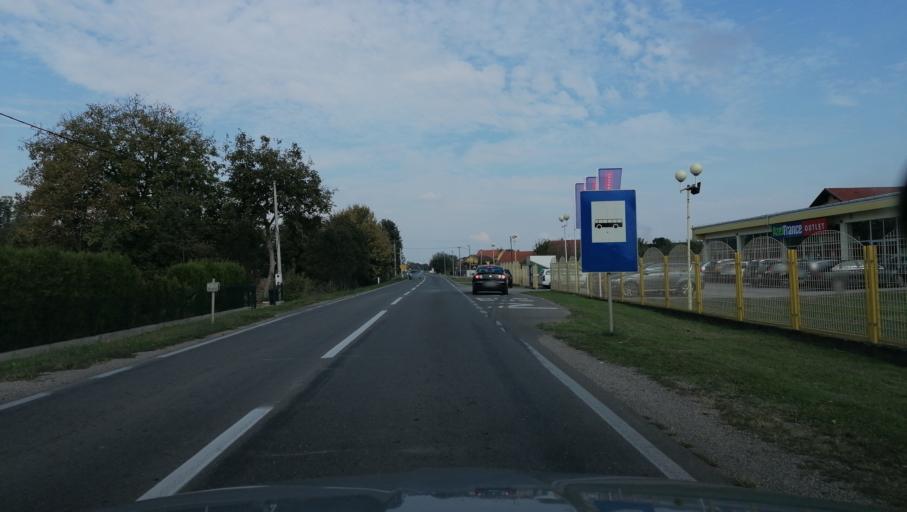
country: BA
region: Republika Srpska
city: Dvorovi
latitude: 44.8190
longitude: 19.2759
